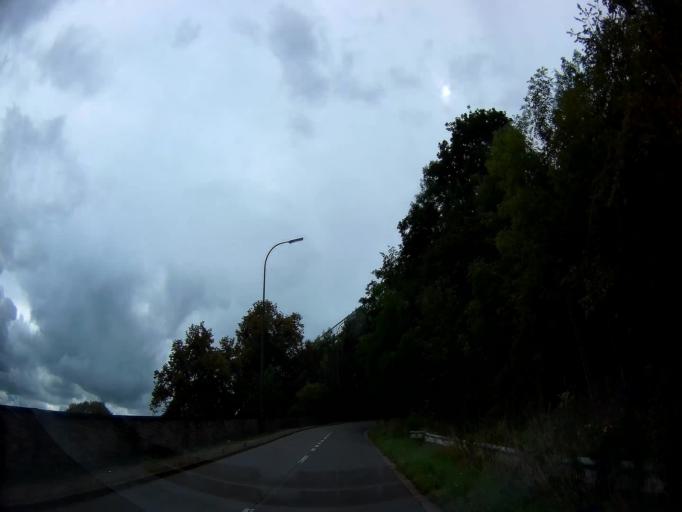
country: BE
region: Wallonia
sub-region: Province de Liege
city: Verviers
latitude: 50.5935
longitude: 5.8447
